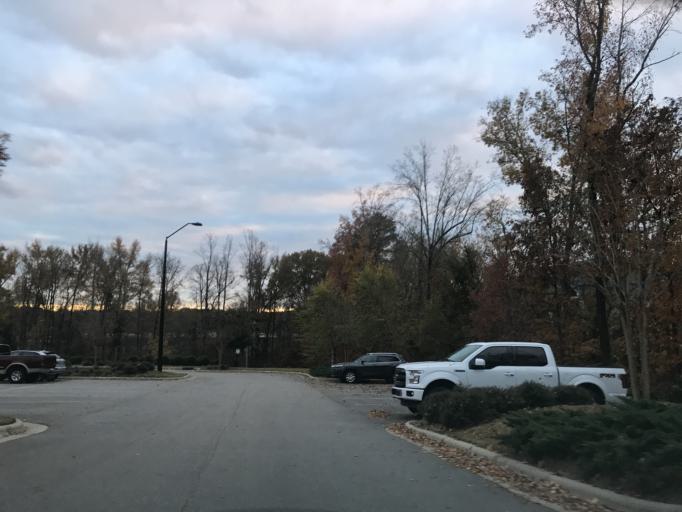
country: US
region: North Carolina
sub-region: Wake County
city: Raleigh
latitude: 35.8163
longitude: -78.6123
